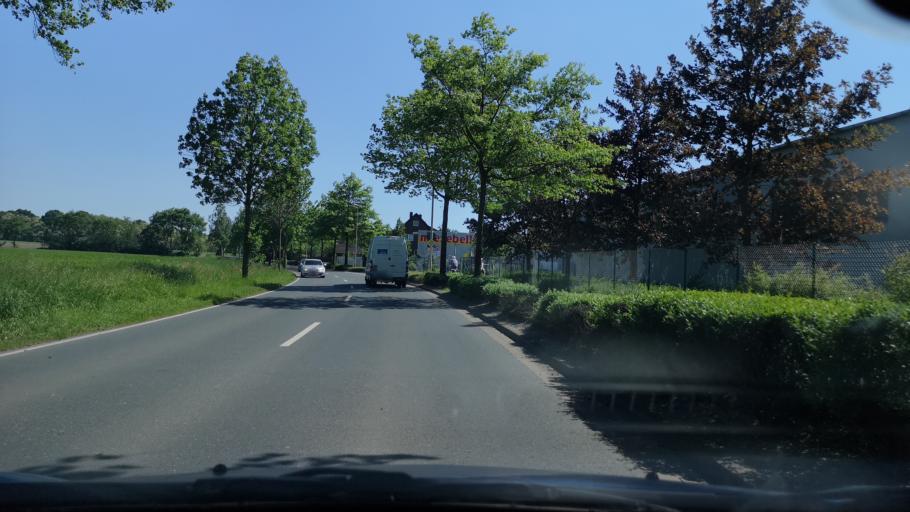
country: DE
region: Lower Saxony
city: Garbsen-Mitte
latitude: 52.4446
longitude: 9.6157
